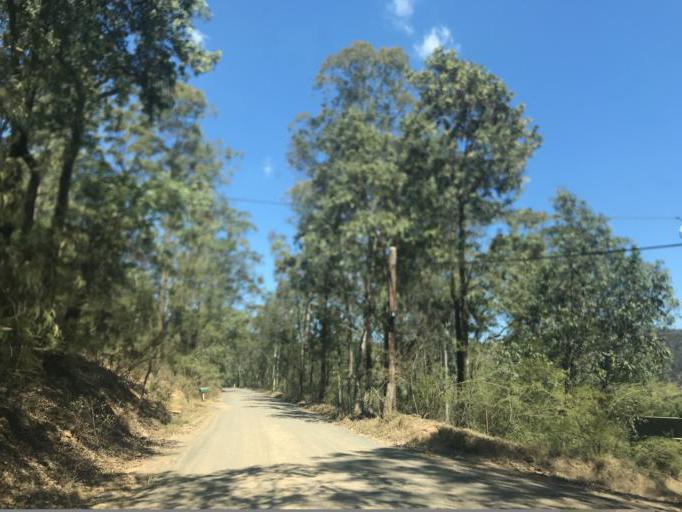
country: AU
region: New South Wales
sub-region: Hornsby Shire
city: Glenorie
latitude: -33.2754
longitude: 150.9674
